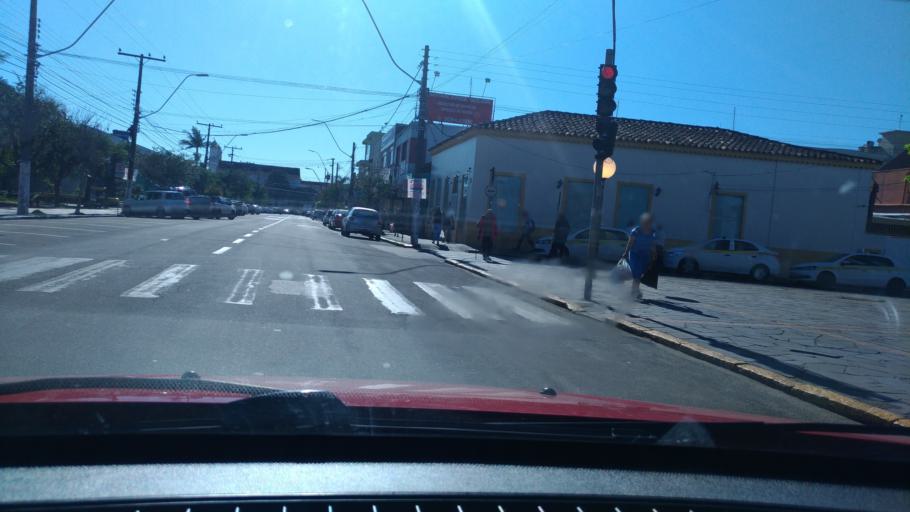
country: BR
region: Rio Grande do Sul
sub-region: Viamao
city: Viamao
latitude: -30.0826
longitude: -51.0269
